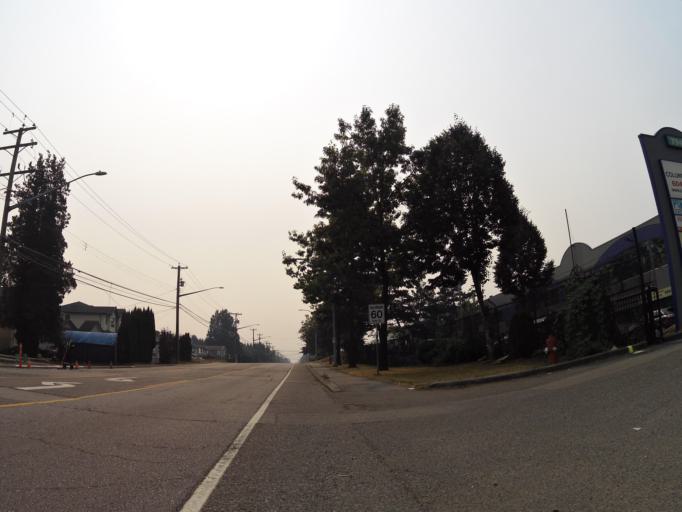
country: CA
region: British Columbia
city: Delta
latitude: 49.1473
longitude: -122.8568
